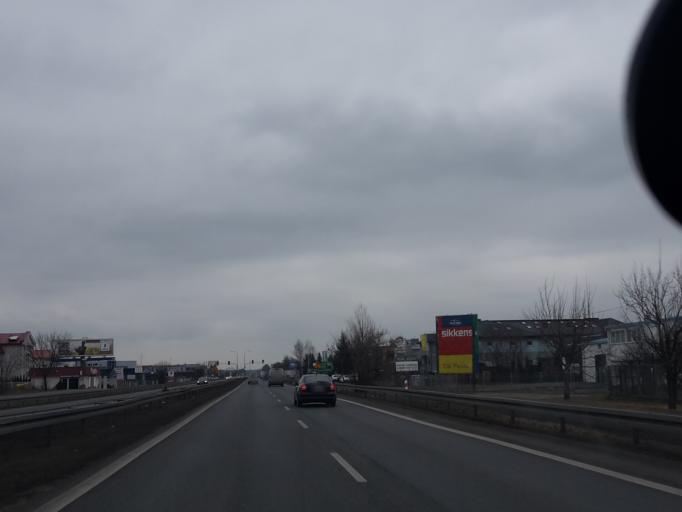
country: PL
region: Masovian Voivodeship
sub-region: Powiat warszawski zachodni
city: Lomianki
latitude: 52.3399
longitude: 20.8697
